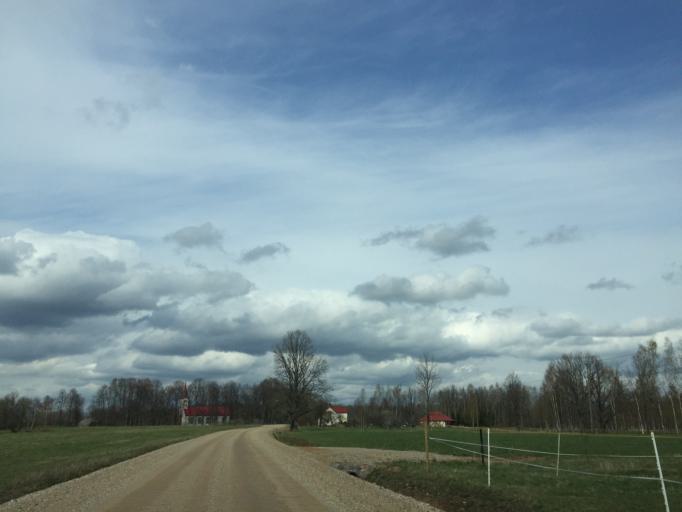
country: LV
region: Ligatne
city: Ligatne
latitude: 57.2138
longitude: 25.0679
